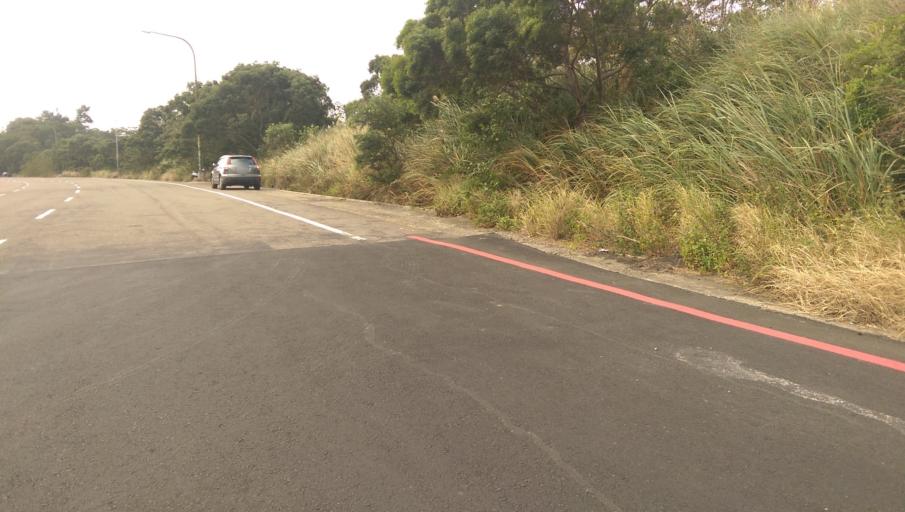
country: TW
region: Taiwan
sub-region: Hsinchu
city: Hsinchu
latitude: 24.7544
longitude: 120.9559
